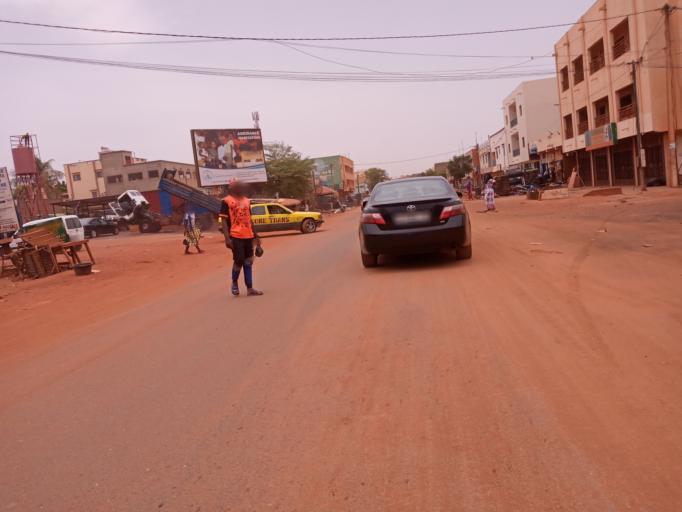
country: ML
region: Bamako
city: Bamako
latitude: 12.5776
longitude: -8.0134
